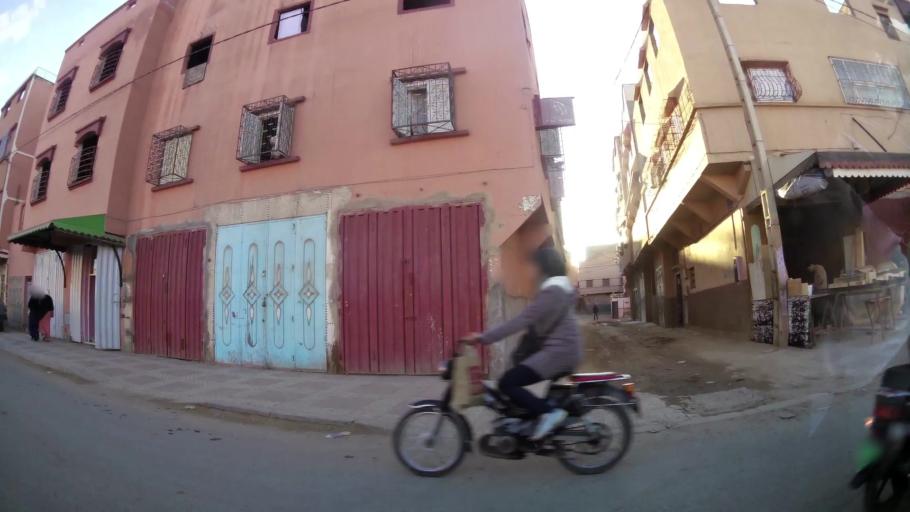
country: MA
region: Marrakech-Tensift-Al Haouz
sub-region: Kelaa-Des-Sraghna
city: Sidi Abdallah
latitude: 32.2416
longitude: -7.9490
